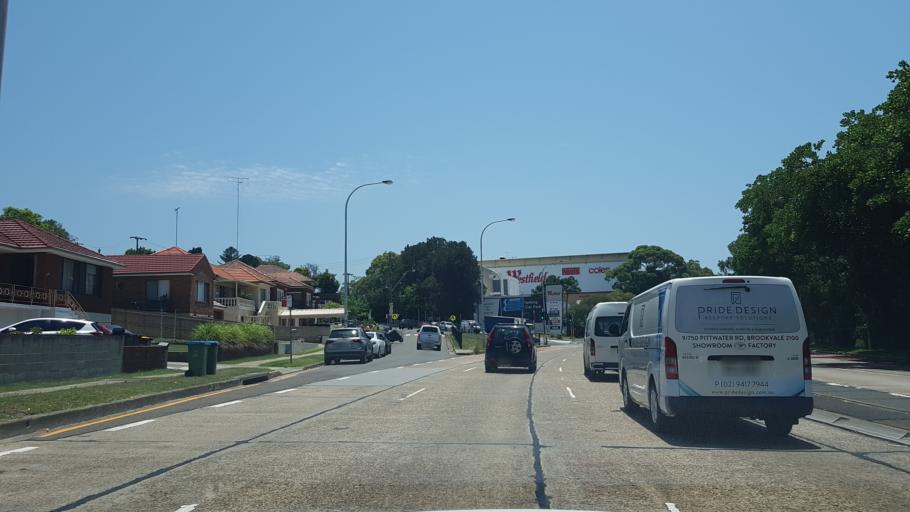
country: AU
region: New South Wales
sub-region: Warringah
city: North Manly
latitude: -33.7713
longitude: 151.2658
